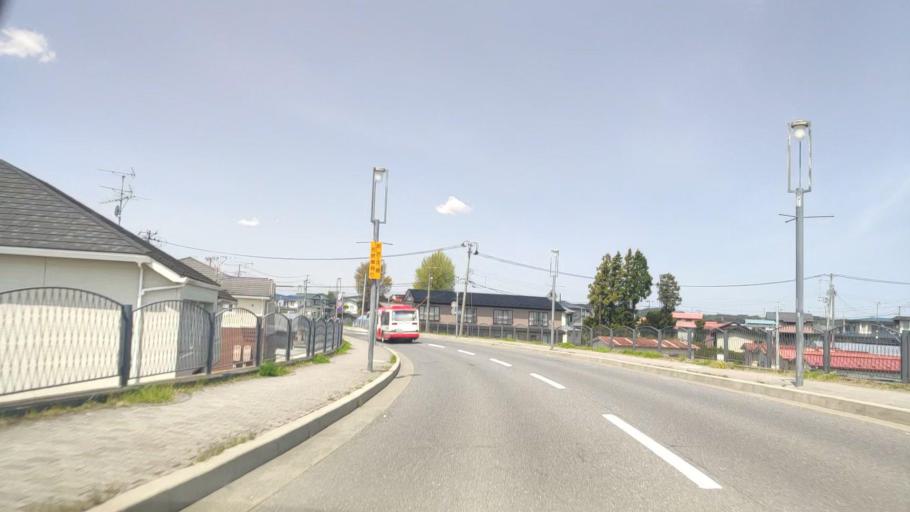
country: JP
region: Aomori
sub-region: Hachinohe Shi
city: Uchimaru
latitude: 40.5025
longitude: 141.4421
